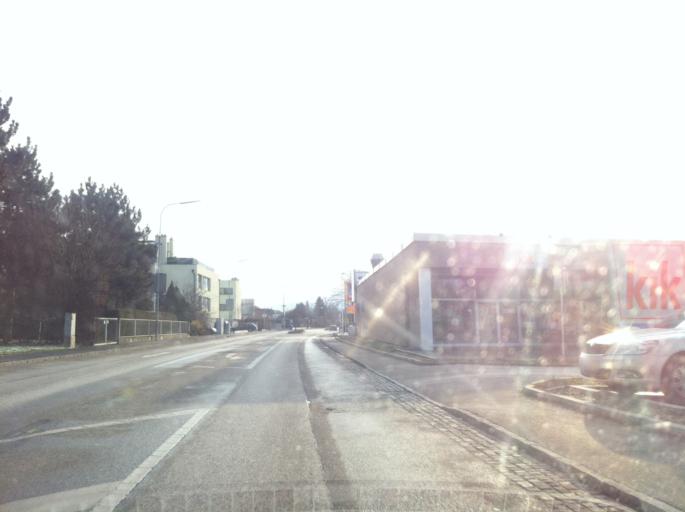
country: AT
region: Lower Austria
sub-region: Politischer Bezirk Tulln
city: Tulln
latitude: 48.3245
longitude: 16.0590
